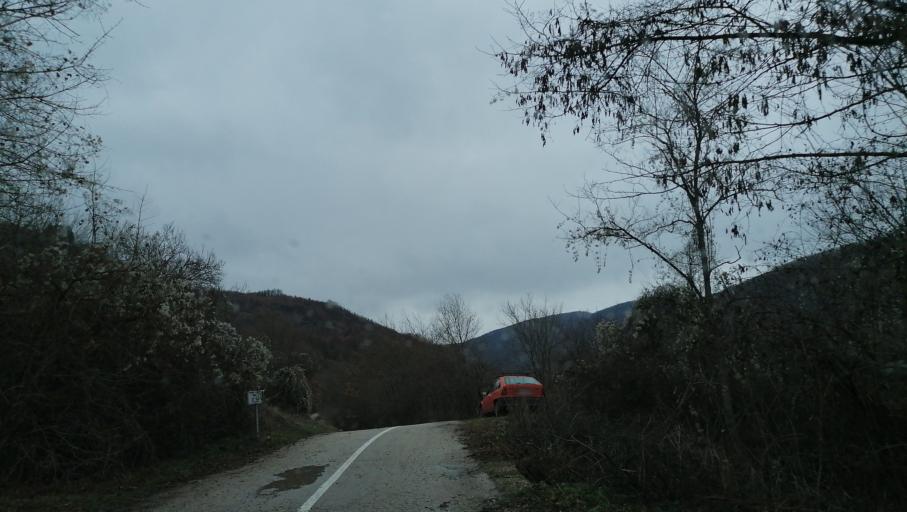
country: RS
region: Central Serbia
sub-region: Pirotski Okrug
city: Dimitrovgrad
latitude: 42.9602
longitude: 22.7826
